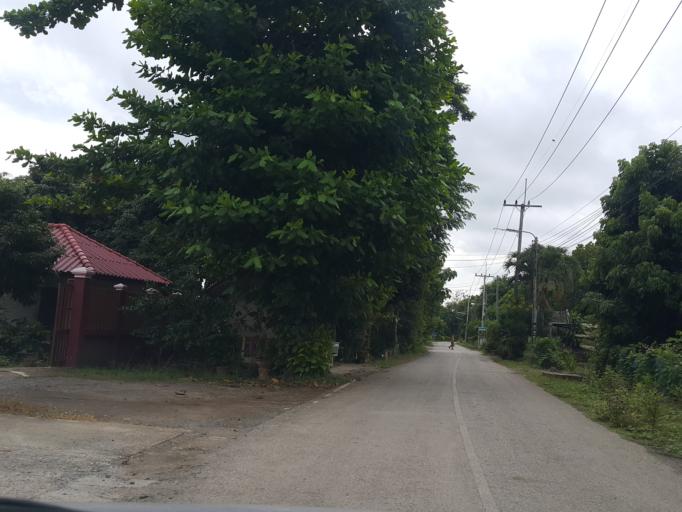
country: TH
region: Chiang Mai
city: San Kamphaeng
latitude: 18.7955
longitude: 99.1402
